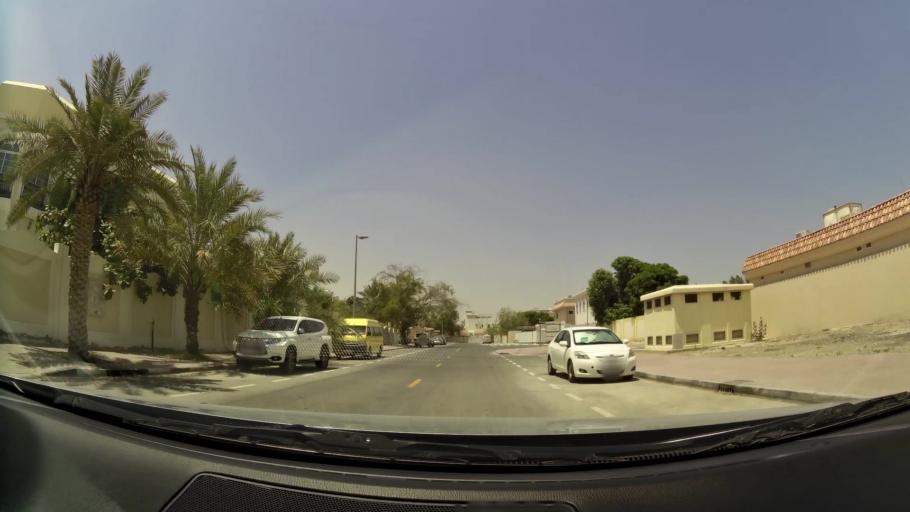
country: AE
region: Dubai
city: Dubai
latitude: 25.1964
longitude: 55.2549
